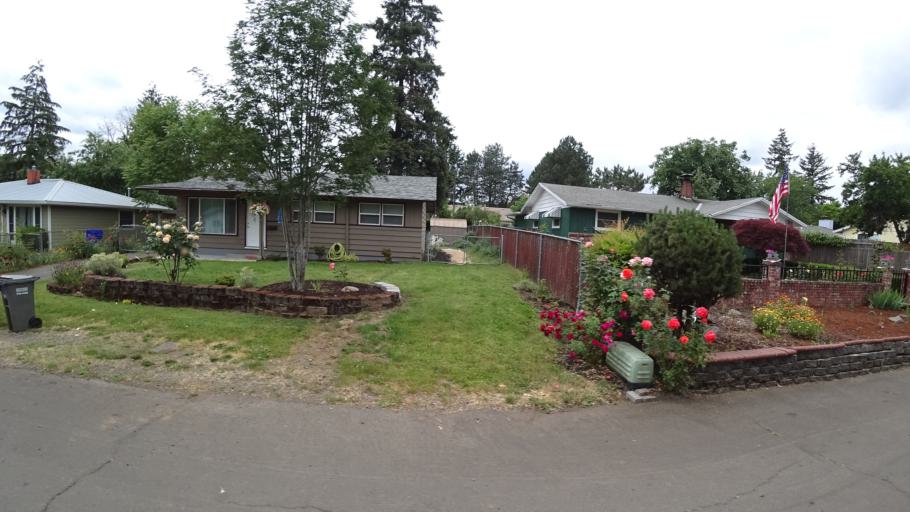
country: US
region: Oregon
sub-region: Multnomah County
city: Lents
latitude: 45.4658
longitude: -122.5823
